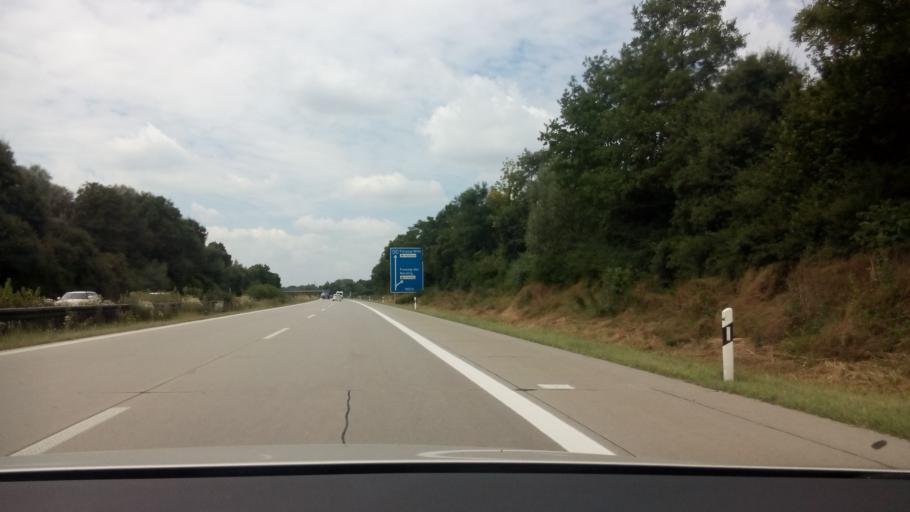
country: DE
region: Bavaria
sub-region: Upper Bavaria
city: Marzling
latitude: 48.3896
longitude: 11.7885
